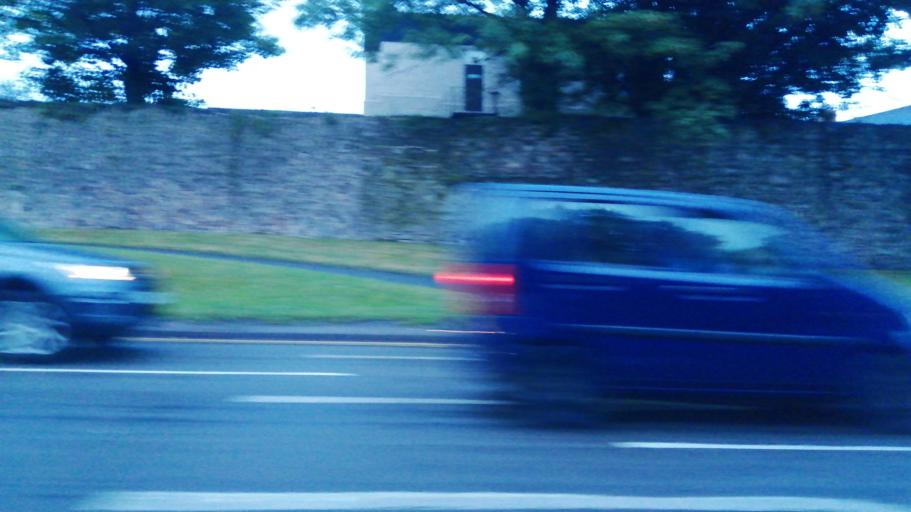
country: GB
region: England
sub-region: Herefordshire
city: Hereford
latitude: 52.0546
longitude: -2.7203
